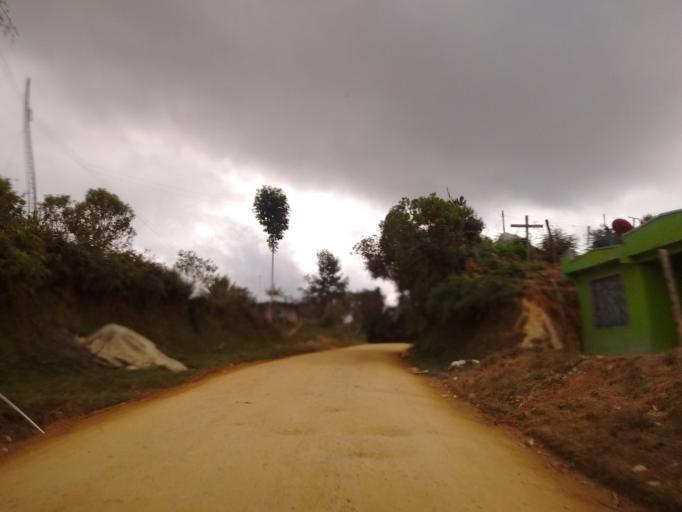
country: CO
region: Huila
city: Isnos
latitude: 2.0239
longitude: -76.2725
